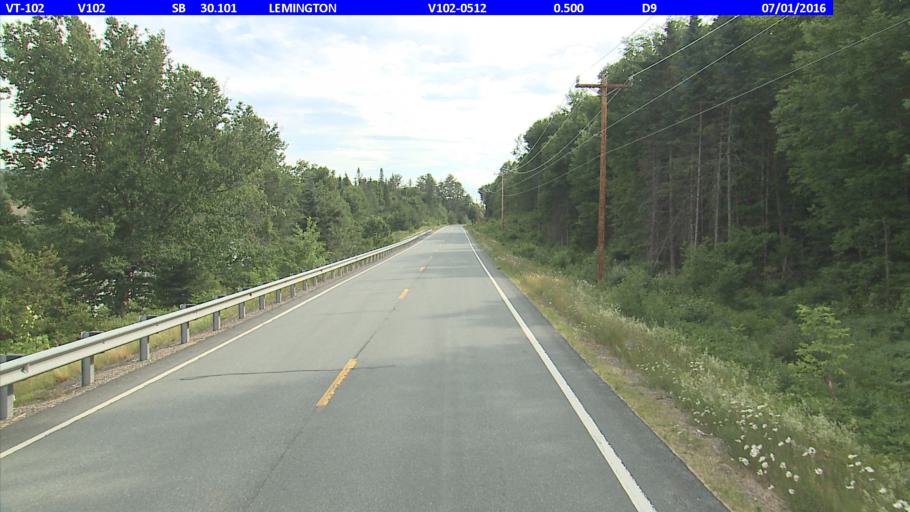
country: US
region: New Hampshire
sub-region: Coos County
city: Colebrook
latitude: 44.8317
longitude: -71.5593
